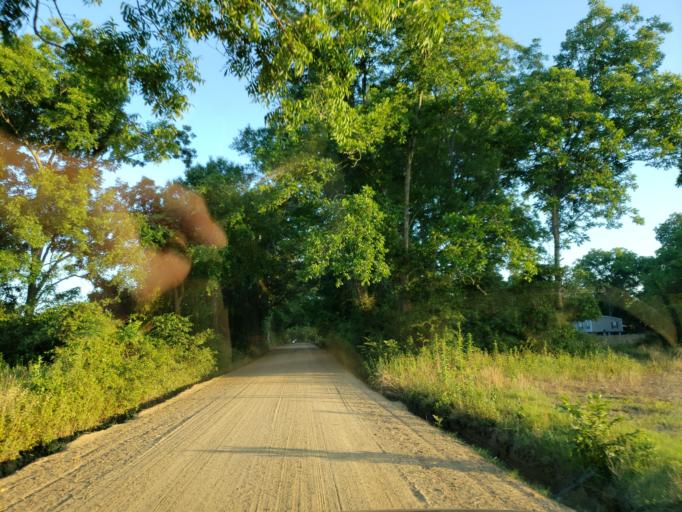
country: US
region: Georgia
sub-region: Crisp County
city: Cordele
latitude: 32.0293
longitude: -83.7484
